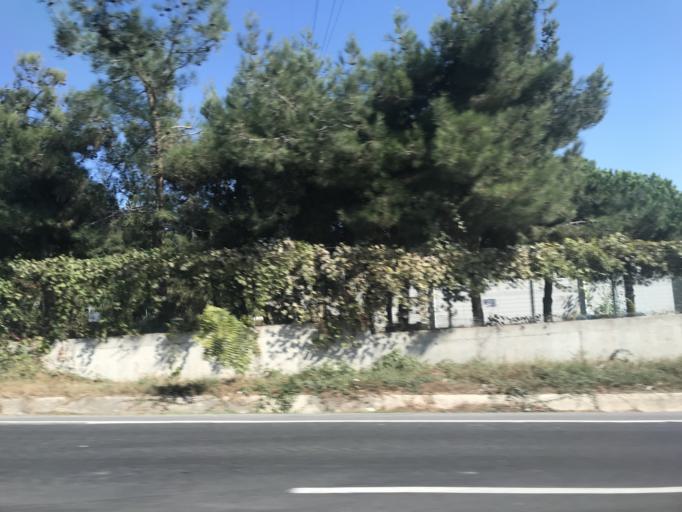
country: TR
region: Tekirdag
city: Tekirdag
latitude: 40.9992
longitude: 27.5102
